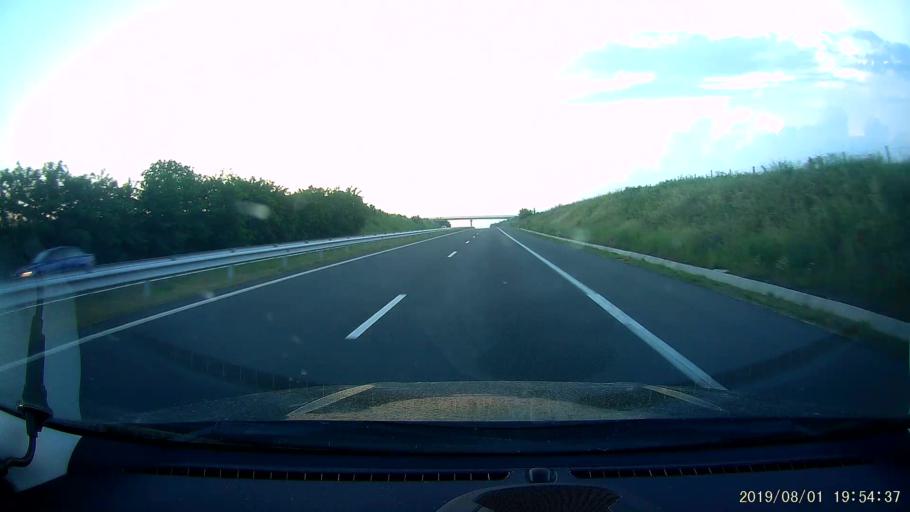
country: BG
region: Burgas
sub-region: Obshtina Karnobat
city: Karnobat
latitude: 42.5755
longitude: 26.8948
